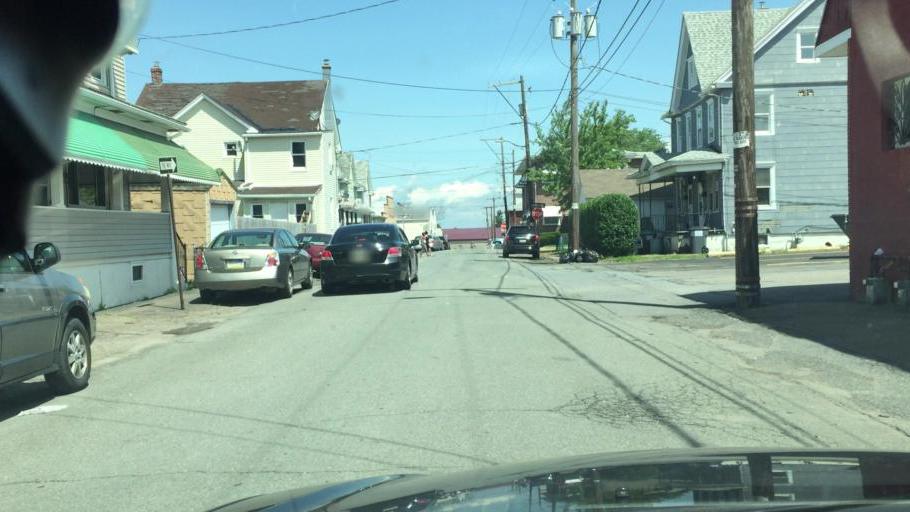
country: US
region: Pennsylvania
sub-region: Luzerne County
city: West Hazleton
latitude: 40.9592
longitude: -75.9964
